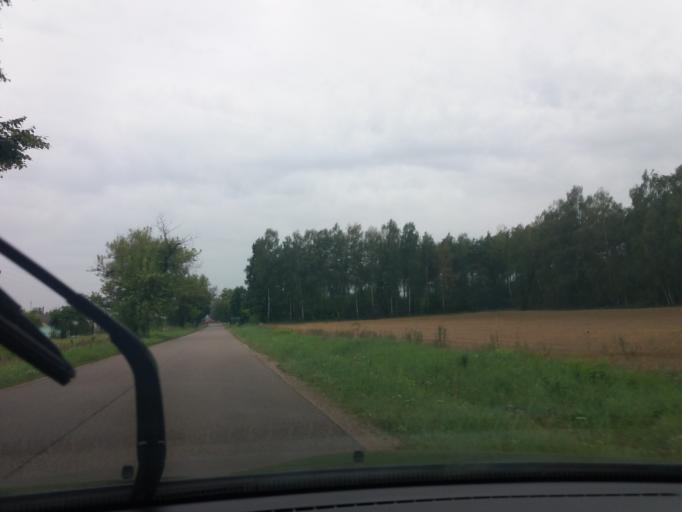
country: PL
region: Masovian Voivodeship
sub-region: Powiat mlawski
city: Wieczfnia Koscielna
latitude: 53.2028
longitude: 20.4926
